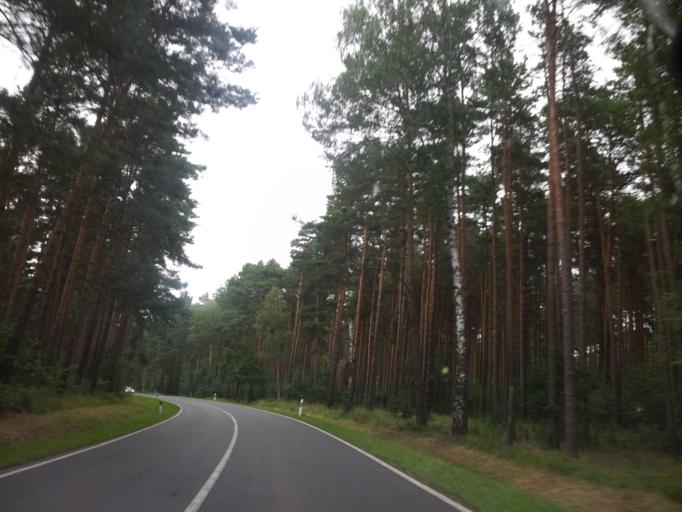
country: DE
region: Brandenburg
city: Niedergorsdorf
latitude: 52.0245
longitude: 12.9494
